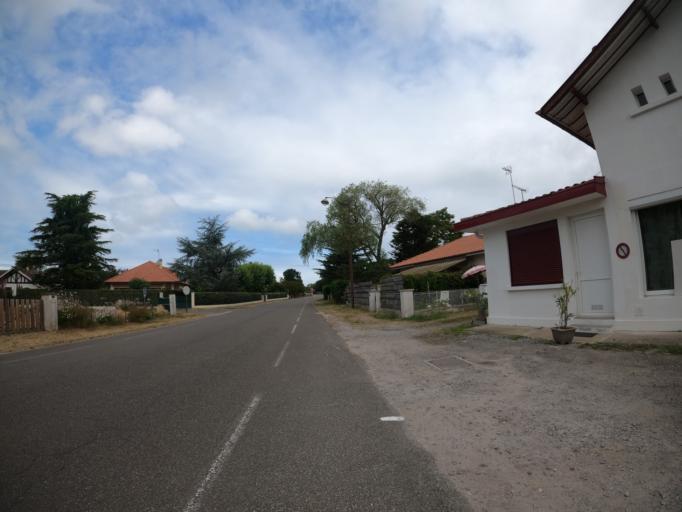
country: FR
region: Aquitaine
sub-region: Departement des Landes
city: Leon
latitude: 43.8801
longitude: -1.3046
